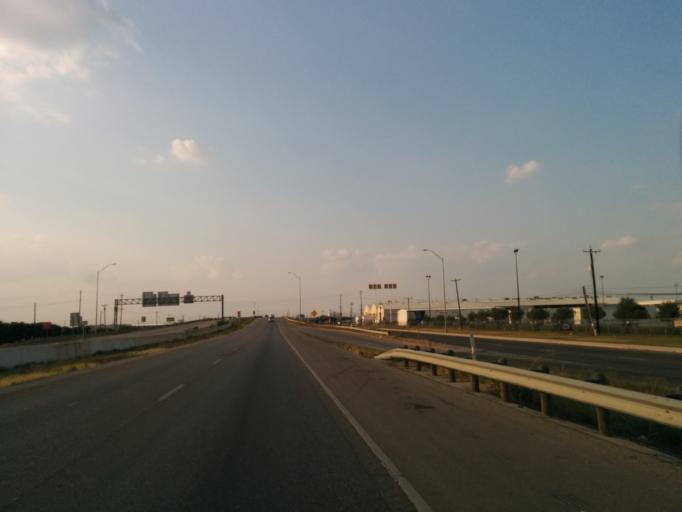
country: US
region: Texas
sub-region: Bexar County
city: Kirby
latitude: 29.4564
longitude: -98.4041
